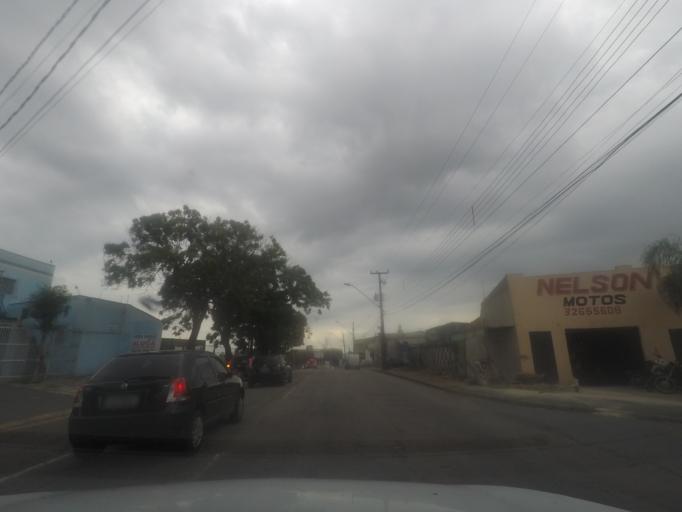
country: BR
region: Parana
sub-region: Sao Jose Dos Pinhais
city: Sao Jose dos Pinhais
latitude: -25.5223
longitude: -49.2971
